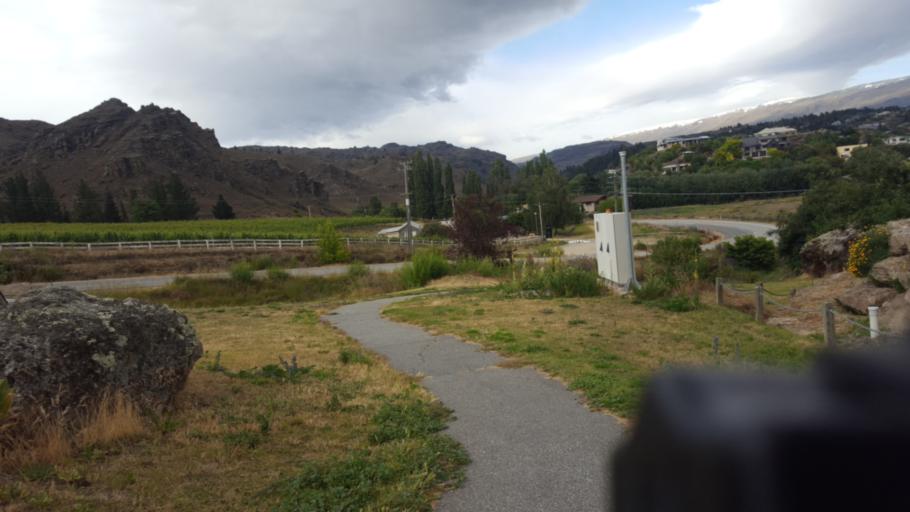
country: NZ
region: Otago
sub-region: Queenstown-Lakes District
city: Wanaka
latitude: -45.2541
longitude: 169.4002
